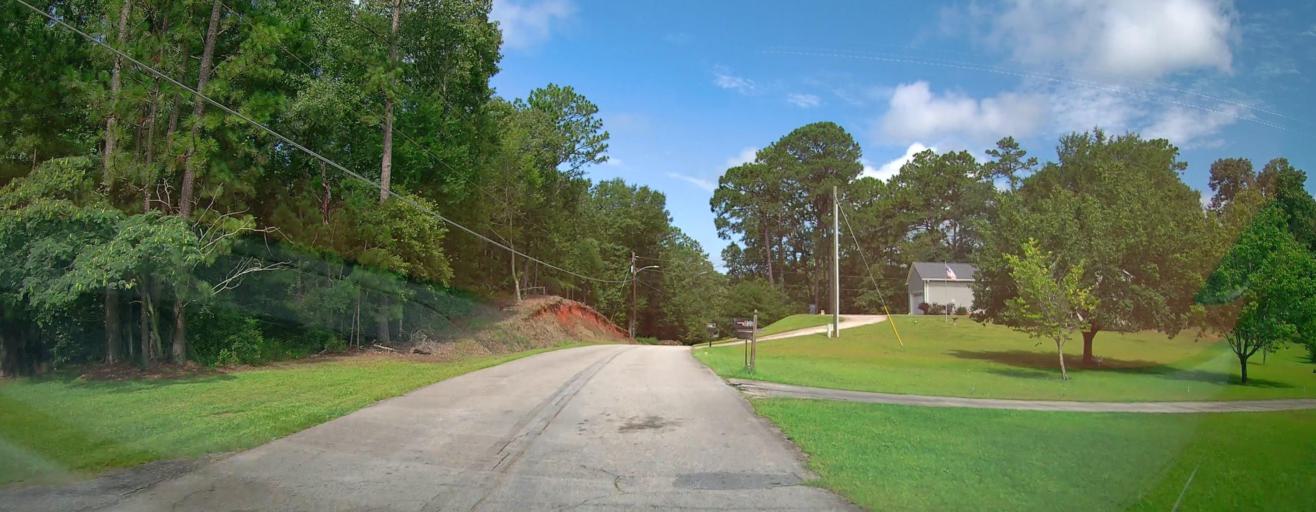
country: US
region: Georgia
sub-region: Peach County
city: Byron
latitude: 32.6599
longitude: -83.7707
